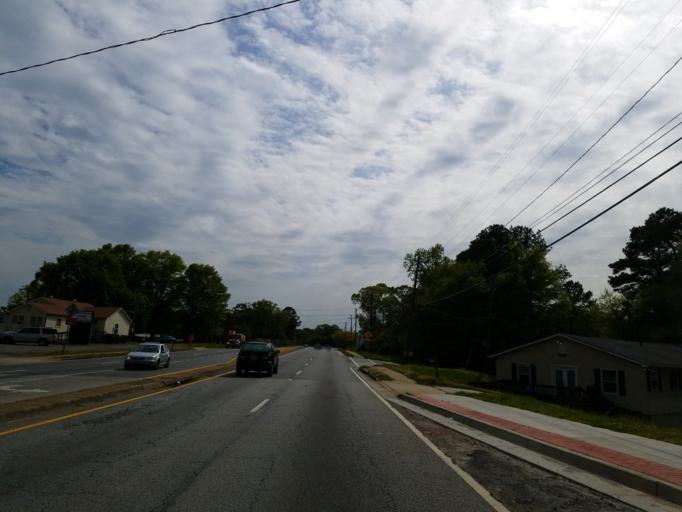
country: US
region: Georgia
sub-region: Cobb County
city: Fair Oaks
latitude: 33.9177
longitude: -84.5508
